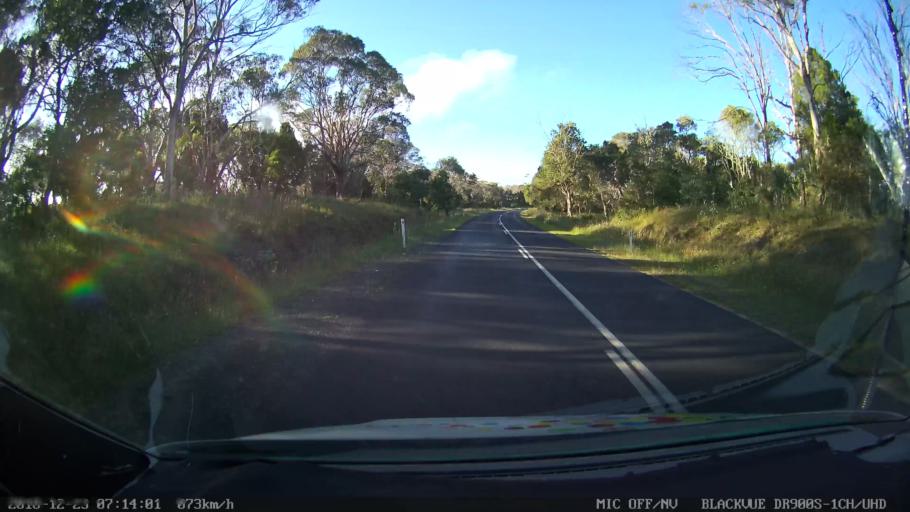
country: AU
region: New South Wales
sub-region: Bellingen
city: Dorrigo
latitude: -30.4306
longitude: 152.3246
